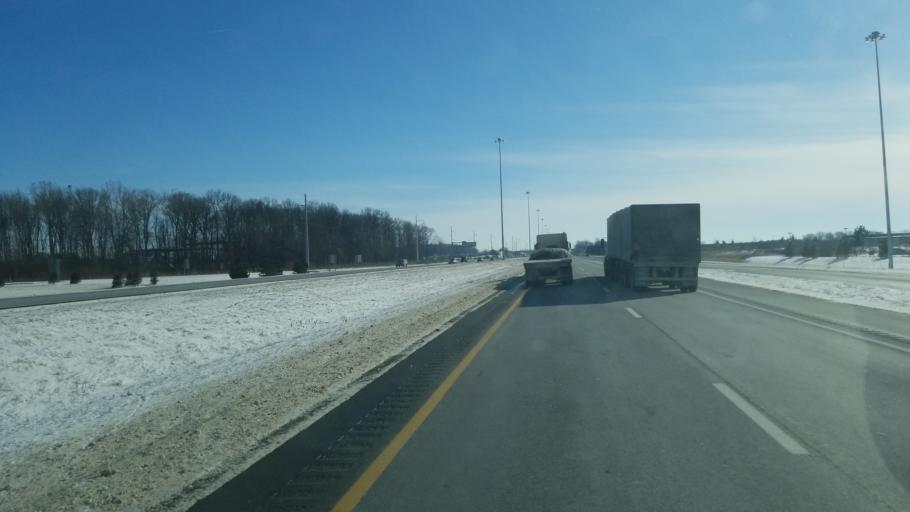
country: US
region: Ohio
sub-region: Lucas County
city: Maumee
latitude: 41.5804
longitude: -83.6914
